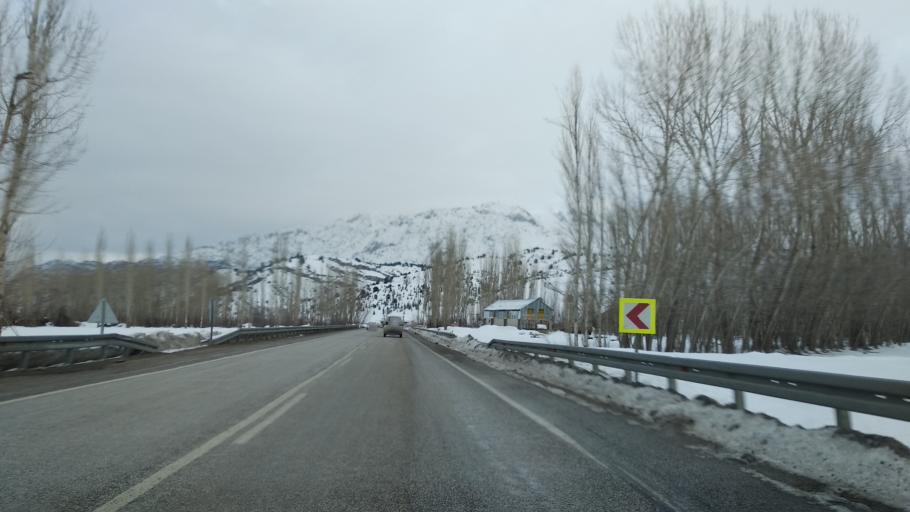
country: TR
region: Kahramanmaras
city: Goksun
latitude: 37.9974
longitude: 36.5254
